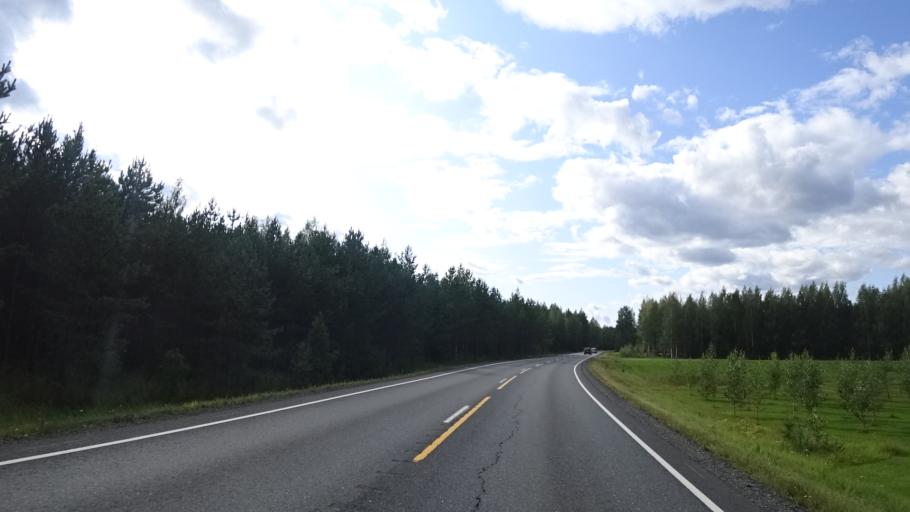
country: FI
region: North Karelia
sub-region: Keski-Karjala
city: Tohmajaervi
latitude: 62.1849
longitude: 30.4733
